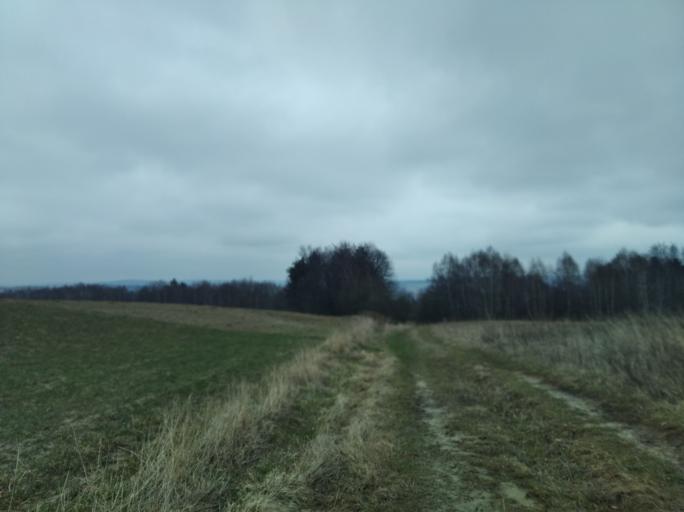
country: PL
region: Subcarpathian Voivodeship
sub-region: Powiat strzyzowski
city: Strzyzow
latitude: 49.9066
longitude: 21.8016
